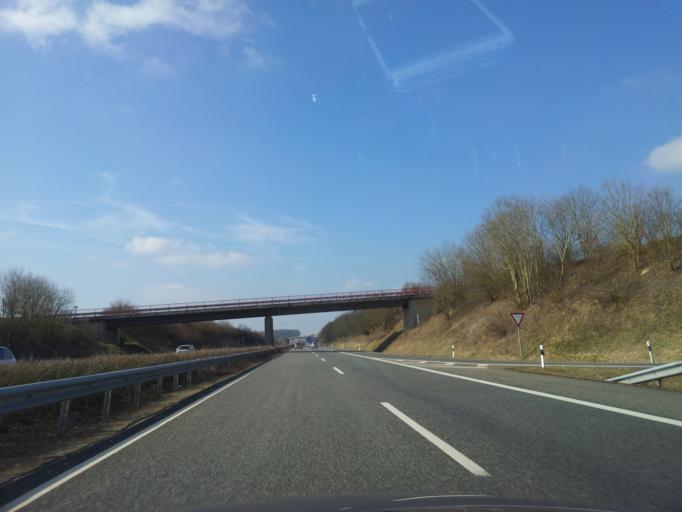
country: DE
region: Rheinland-Pfalz
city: Gindorf
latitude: 50.0205
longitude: 6.6332
